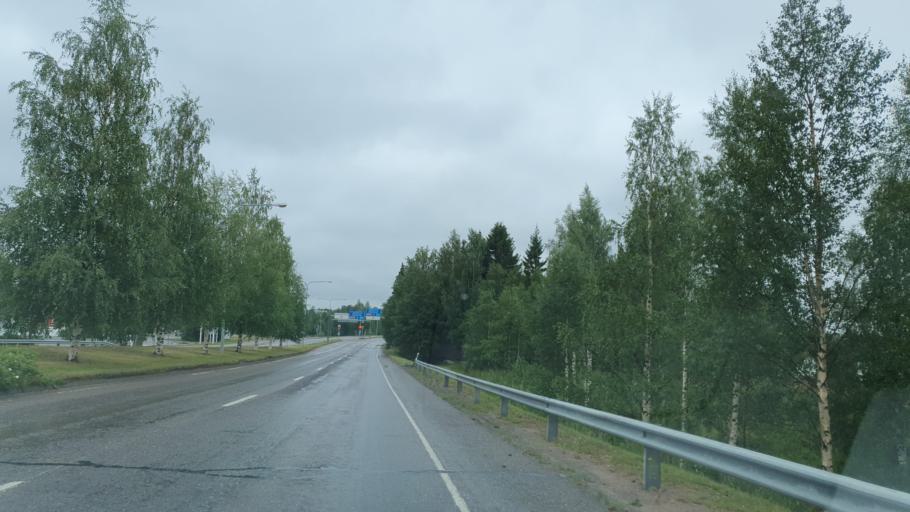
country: FI
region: Lapland
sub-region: Itae-Lappi
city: Kemijaervi
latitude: 66.7185
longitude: 27.4192
